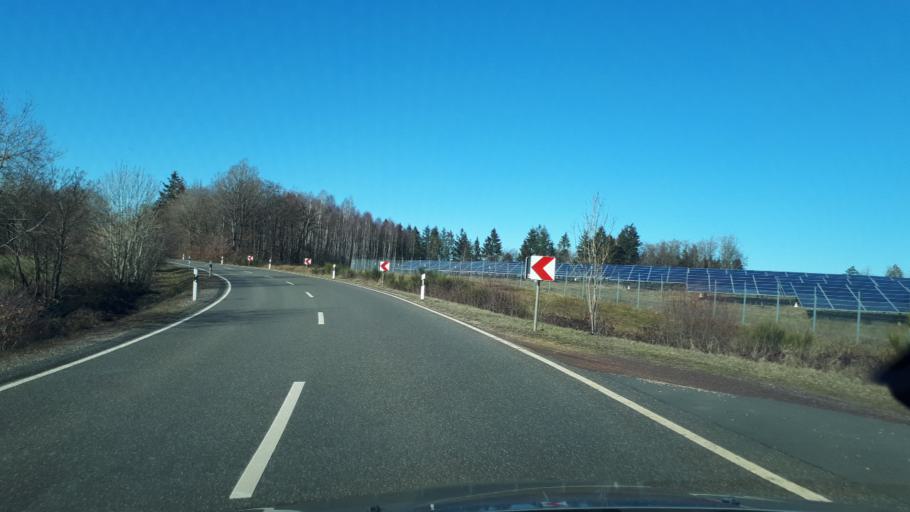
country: DE
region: Rheinland-Pfalz
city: Ellscheid
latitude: 50.1545
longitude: 6.9289
